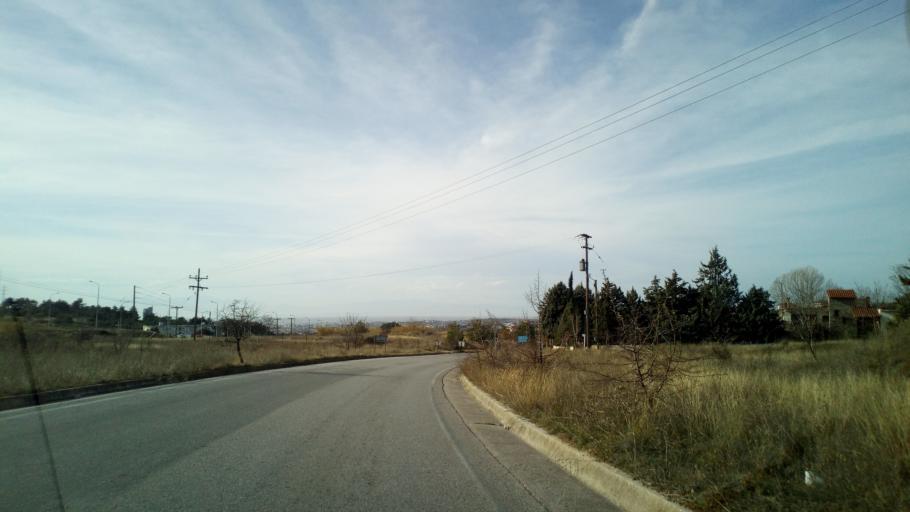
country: GR
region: Central Macedonia
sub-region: Nomos Thessalonikis
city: Liti
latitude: 40.7196
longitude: 22.9687
